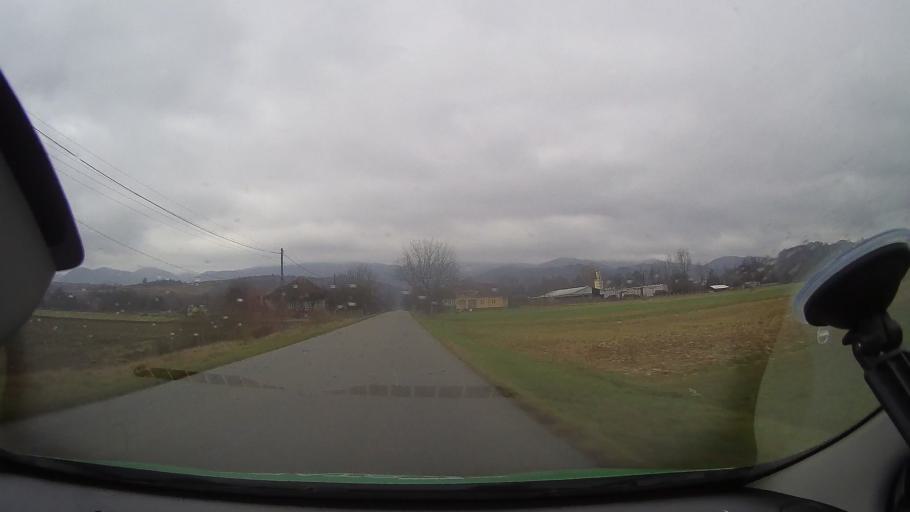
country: RO
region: Hunedoara
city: Vata de Jos
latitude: 46.1895
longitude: 22.6071
